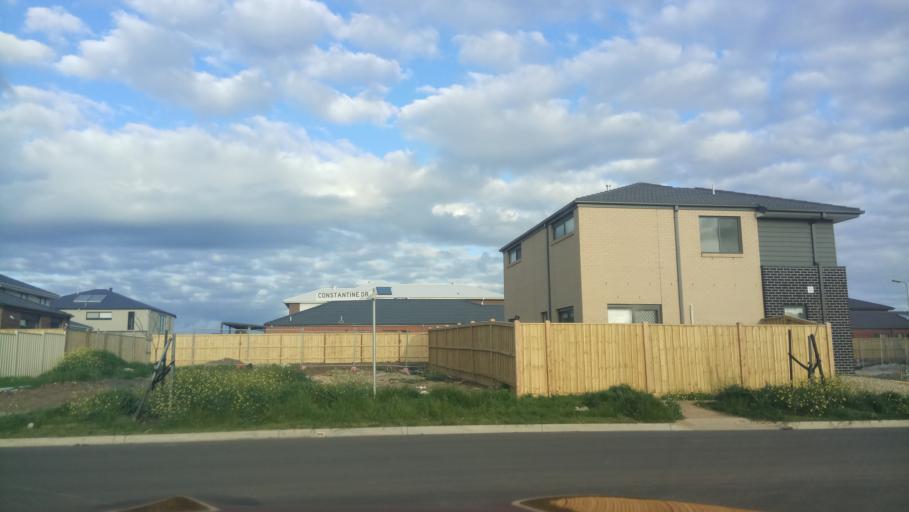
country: AU
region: Victoria
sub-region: Wyndham
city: Point Cook
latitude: -37.9130
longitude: 144.7499
